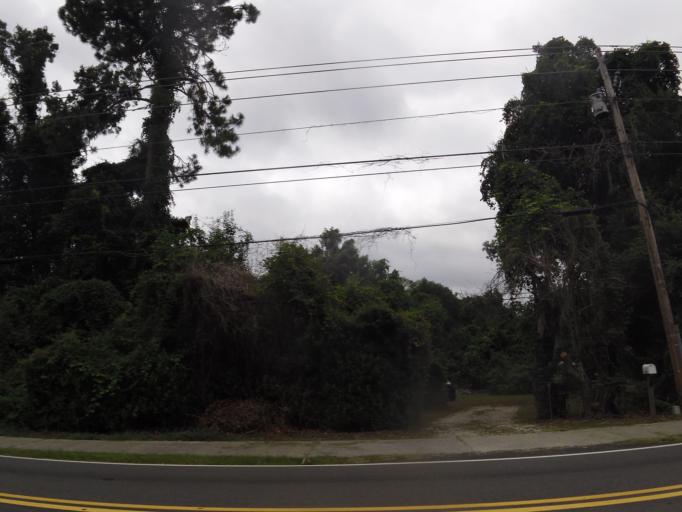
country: US
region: Georgia
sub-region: Glynn County
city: Saint Simon Mills
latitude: 31.1615
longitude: -81.3948
